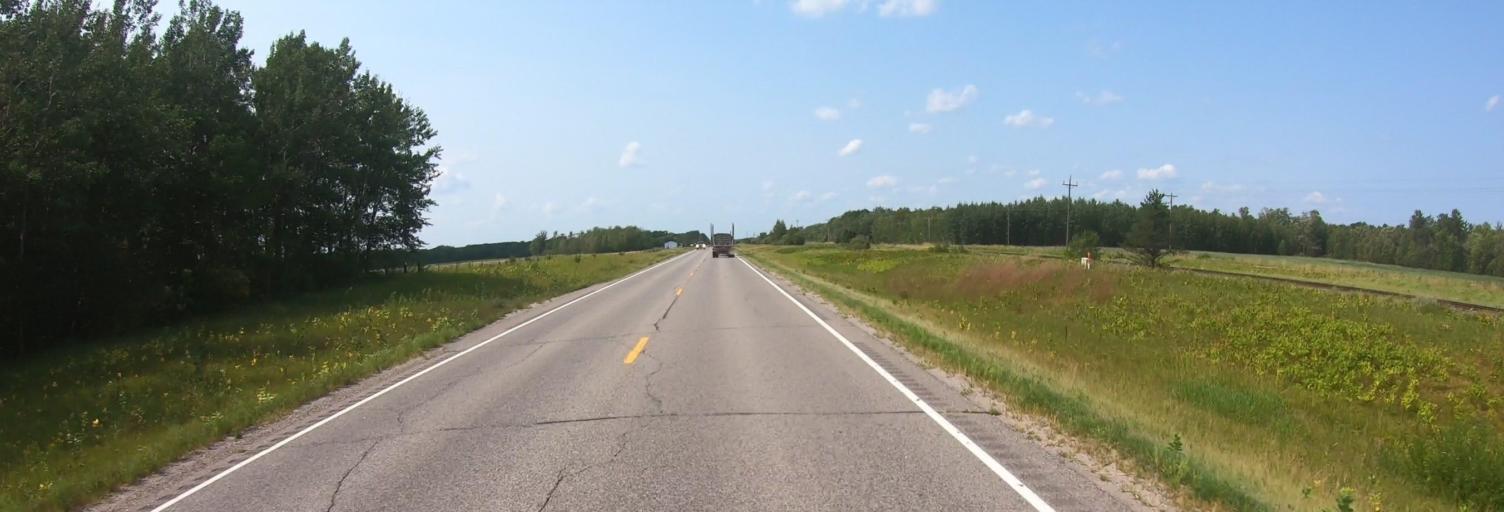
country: US
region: Minnesota
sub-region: Roseau County
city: Warroad
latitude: 48.8329
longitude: -95.1723
